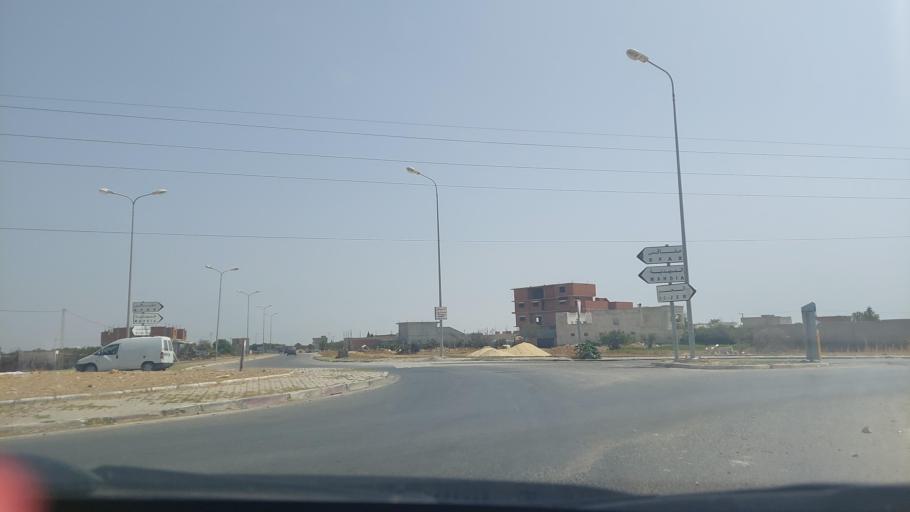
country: TN
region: Al Munastir
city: Qasr Hallal
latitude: 35.6040
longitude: 10.8904
